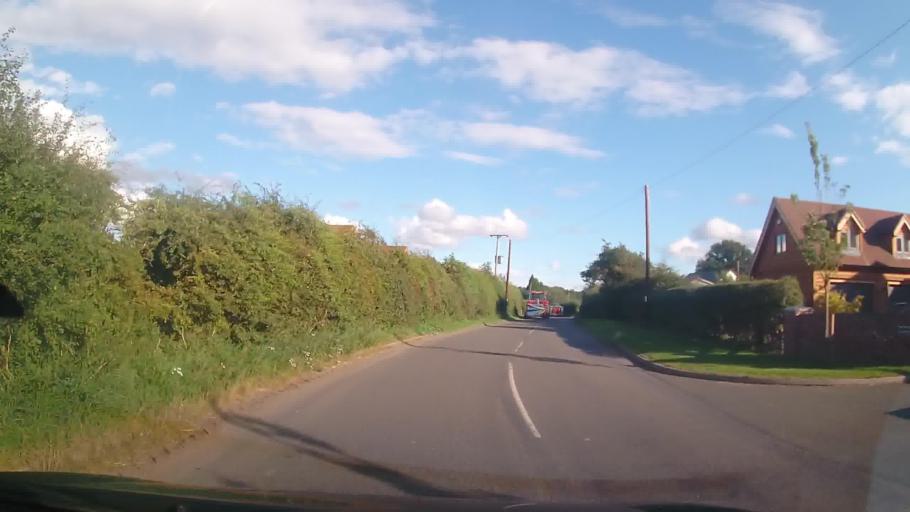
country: GB
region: England
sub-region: Shropshire
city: Great Hanwood
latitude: 52.6530
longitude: -2.8037
